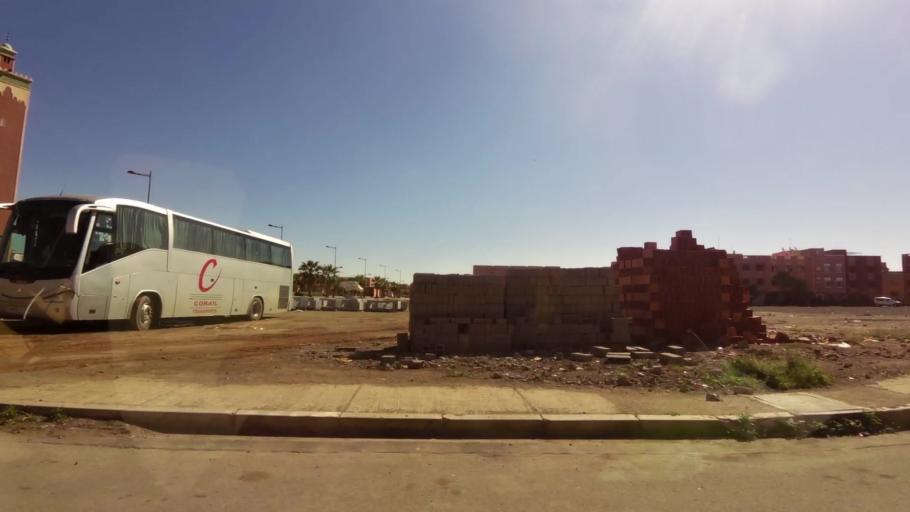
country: MA
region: Marrakech-Tensift-Al Haouz
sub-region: Marrakech
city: Marrakesh
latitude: 31.5891
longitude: -8.0556
